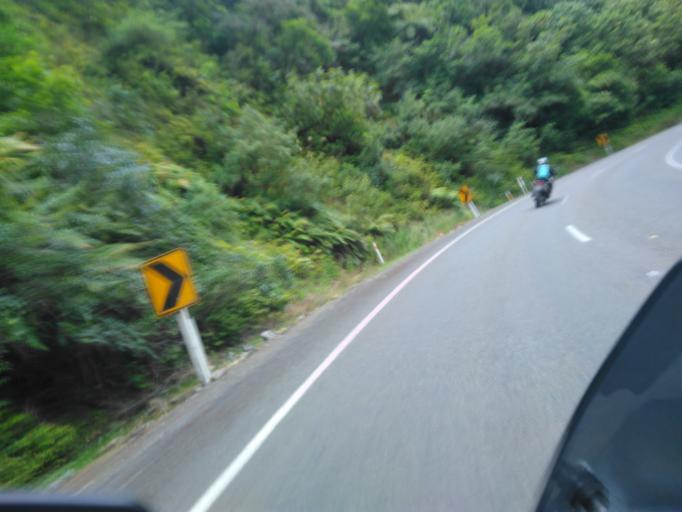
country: NZ
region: Bay of Plenty
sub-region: Opotiki District
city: Opotiki
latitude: -38.2690
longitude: 177.3183
